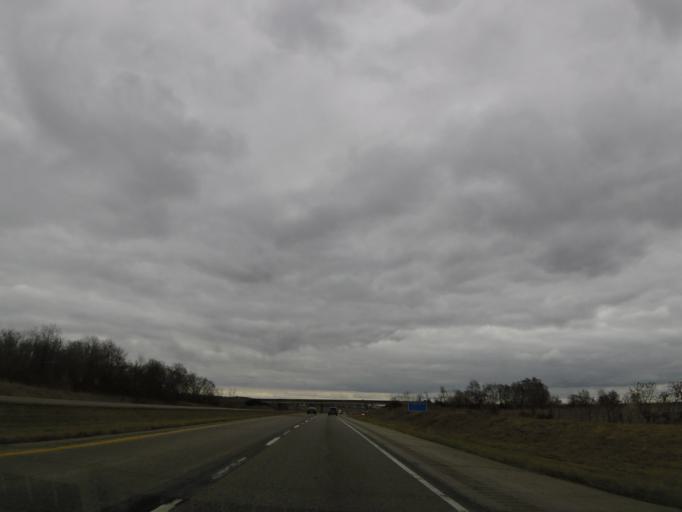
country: US
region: Iowa
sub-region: Linn County
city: Center Point
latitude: 42.1873
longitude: -91.8043
